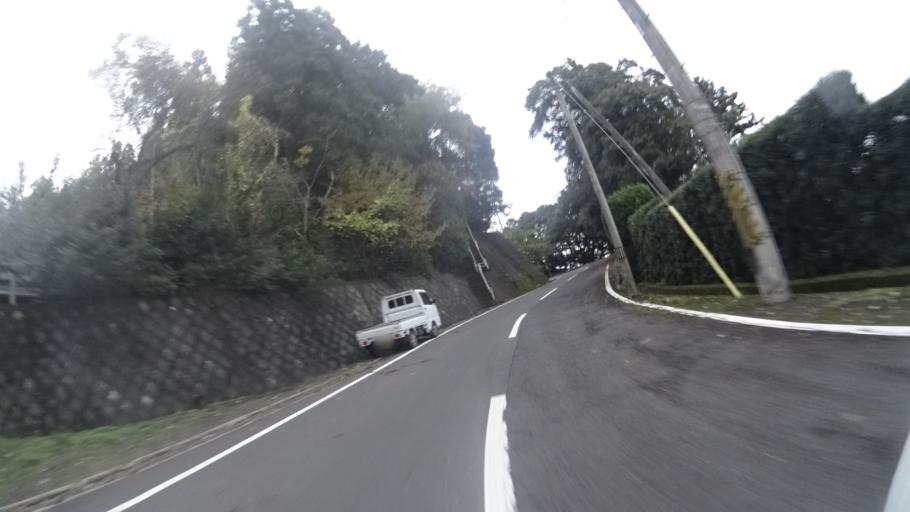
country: JP
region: Kyoto
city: Maizuru
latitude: 35.5666
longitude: 135.4526
